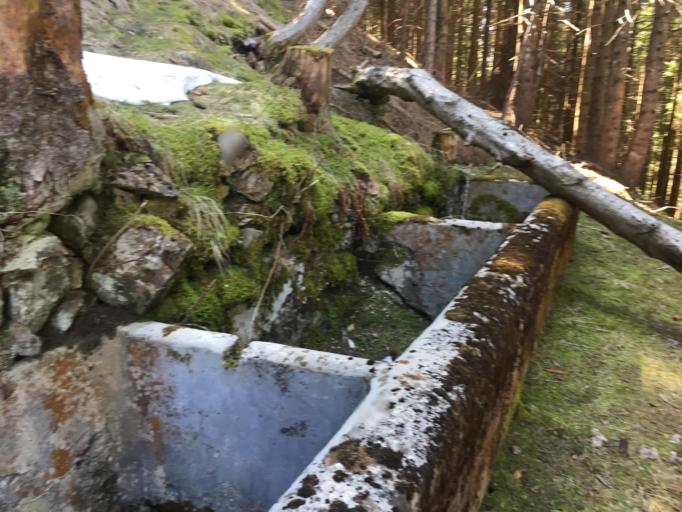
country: IT
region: Friuli Venezia Giulia
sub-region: Provincia di Udine
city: Paularo
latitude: 46.5099
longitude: 13.1728
